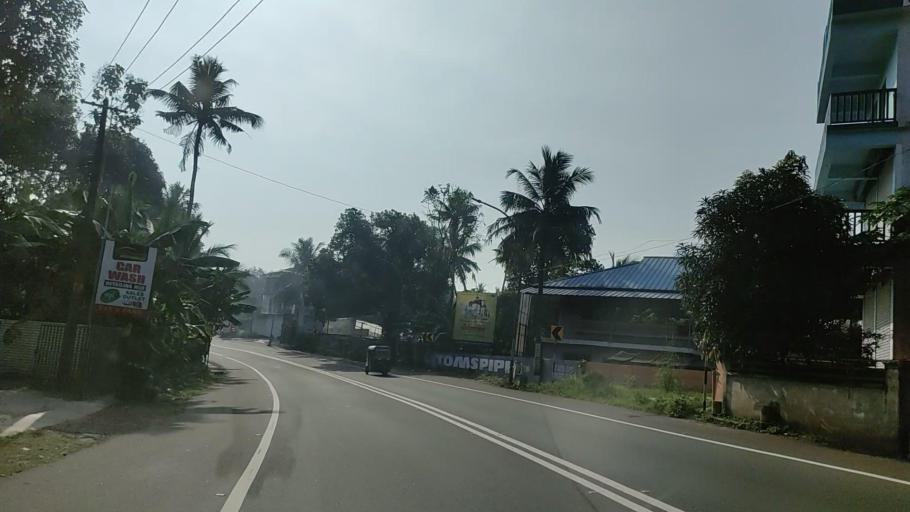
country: IN
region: Kerala
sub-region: Kollam
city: Punalur
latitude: 8.9798
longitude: 76.8108
